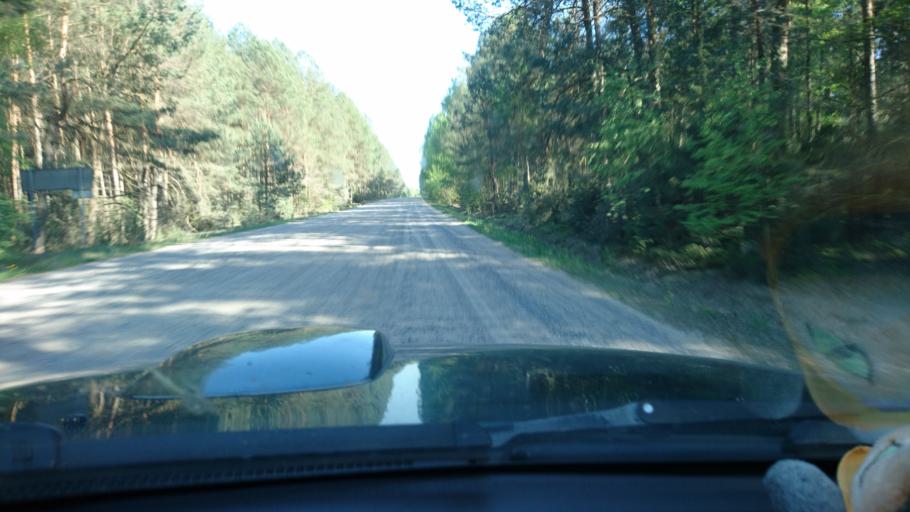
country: BY
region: Brest
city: Zhabinka
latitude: 52.3833
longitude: 24.1153
